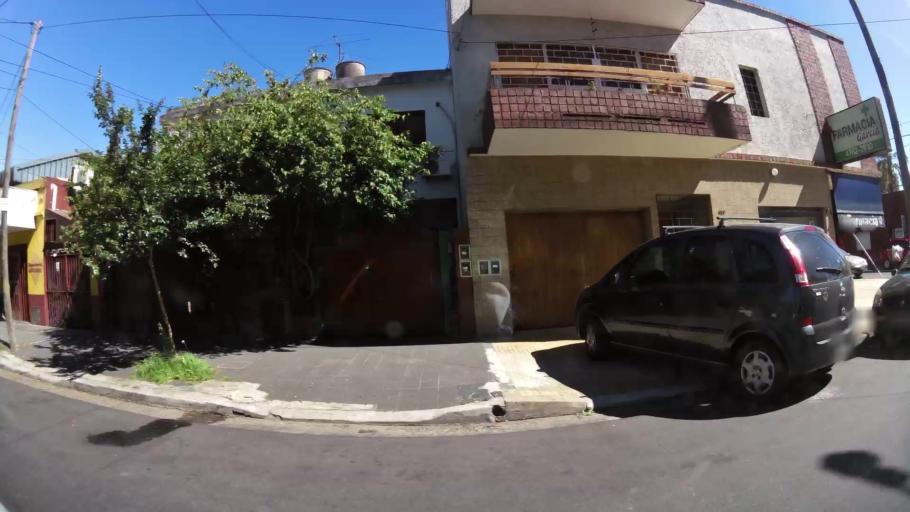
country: AR
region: Buenos Aires
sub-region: Partido de Vicente Lopez
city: Olivos
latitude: -34.5281
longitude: -58.5129
